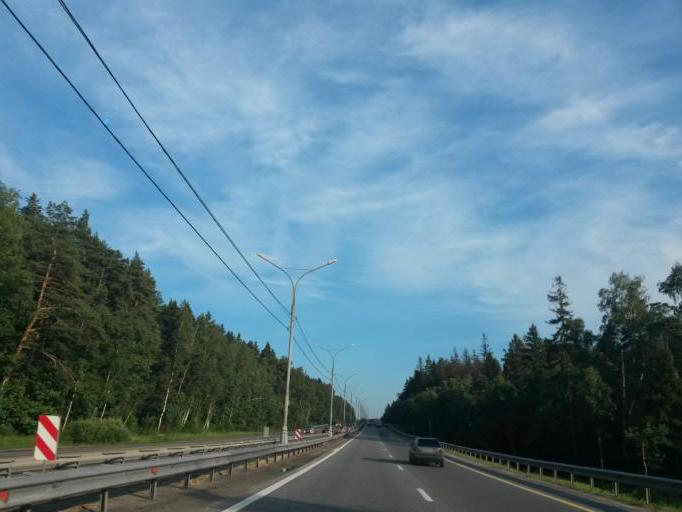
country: RU
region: Moskovskaya
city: Vostryakovo
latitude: 55.4507
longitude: 37.8591
